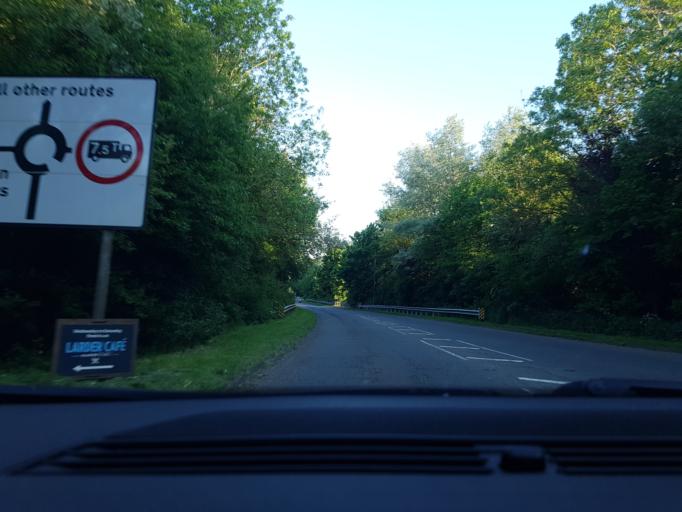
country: GB
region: England
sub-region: Buckinghamshire
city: Buckingham
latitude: 51.9960
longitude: -0.9699
